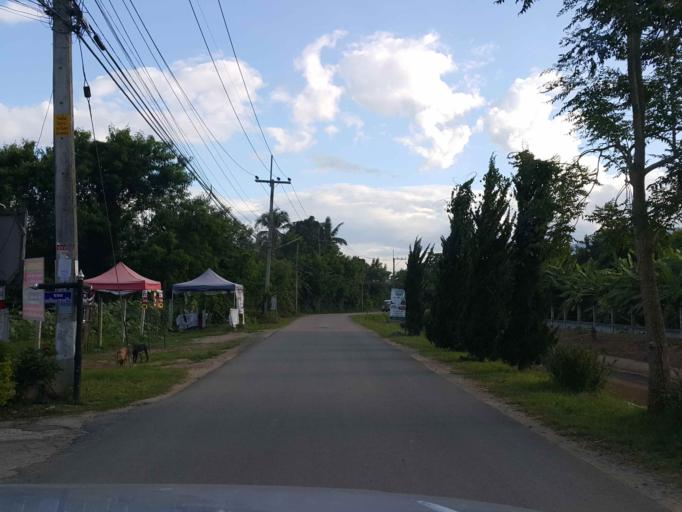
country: TH
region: Chiang Mai
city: San Sai
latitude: 18.9224
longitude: 98.9754
